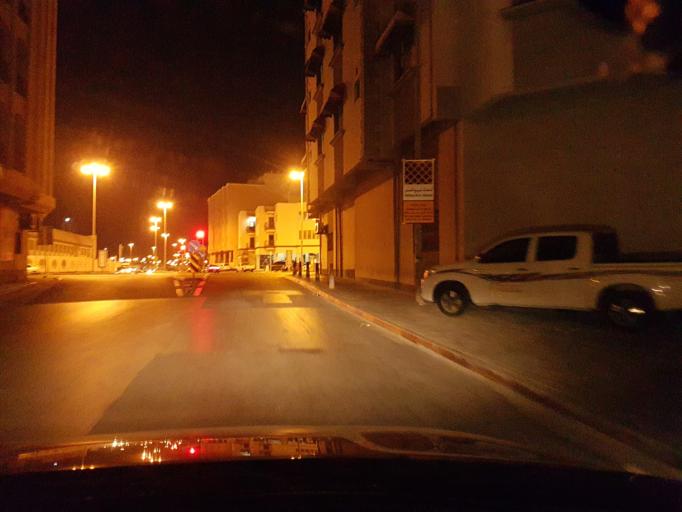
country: BH
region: Manama
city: Jidd Hafs
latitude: 26.2242
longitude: 50.5653
